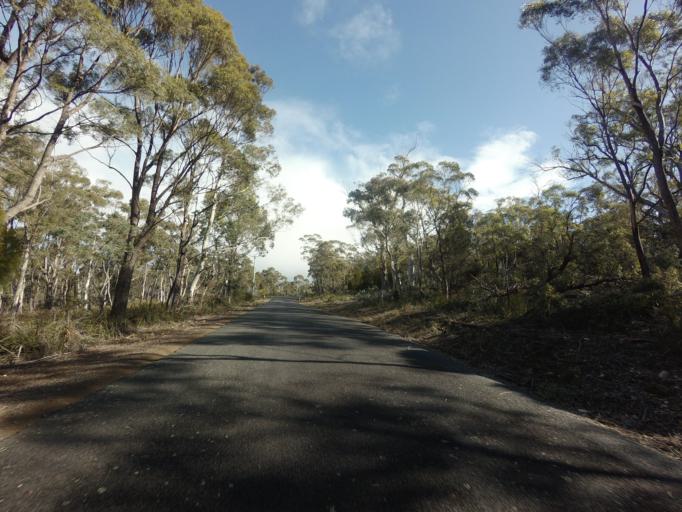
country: AU
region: Tasmania
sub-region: Sorell
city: Sorell
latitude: -42.3611
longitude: 147.9556
